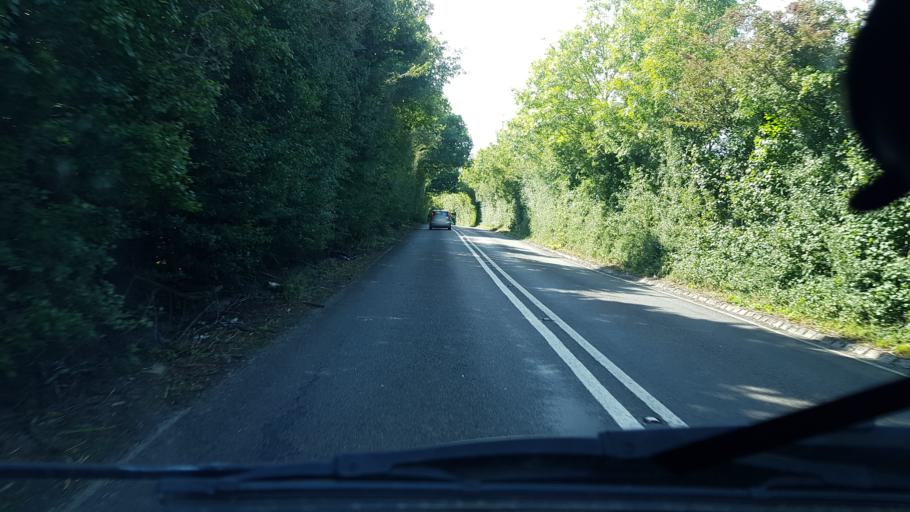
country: GB
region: England
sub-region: West Sussex
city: Rudgwick
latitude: 51.0864
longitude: -0.4340
